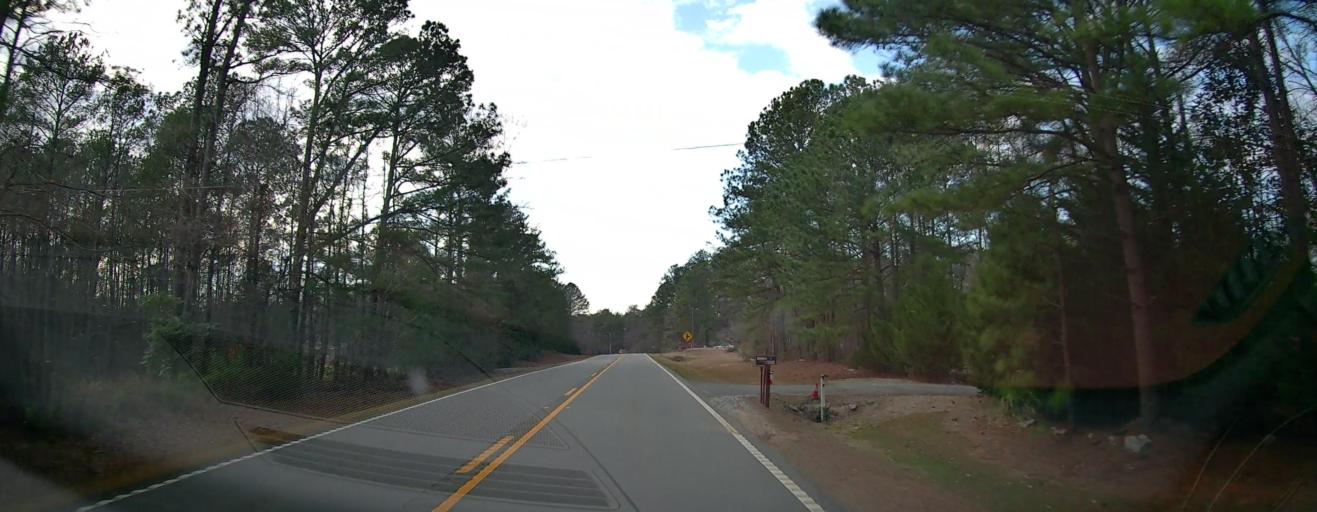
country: US
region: Georgia
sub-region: Harris County
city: Hamilton
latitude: 32.7017
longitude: -84.8163
